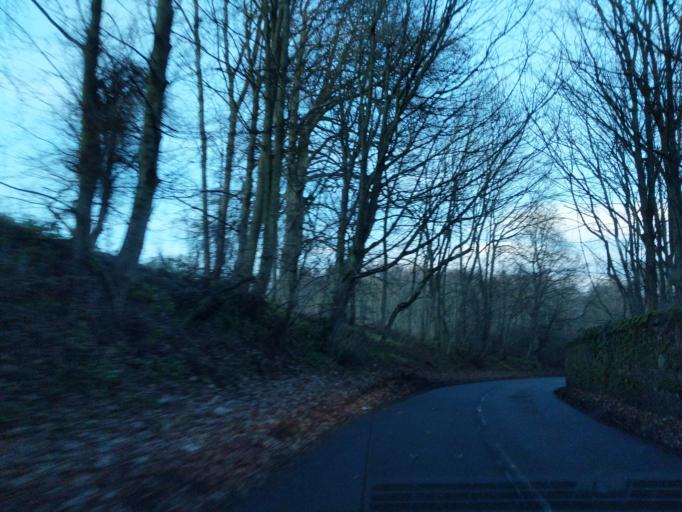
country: GB
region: Scotland
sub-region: Midlothian
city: Gorebridge
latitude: 55.8216
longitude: -3.0885
